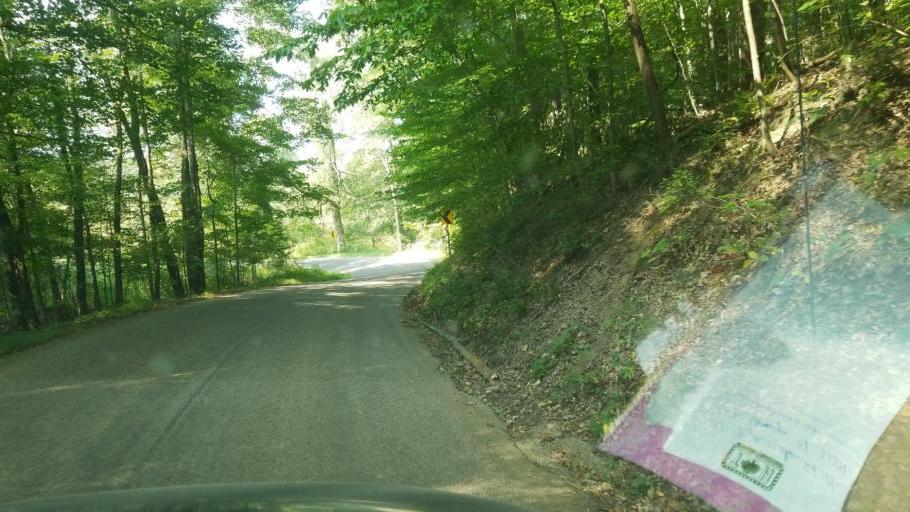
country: US
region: Ohio
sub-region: Sandusky County
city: Bellville
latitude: 40.5901
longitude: -82.4469
